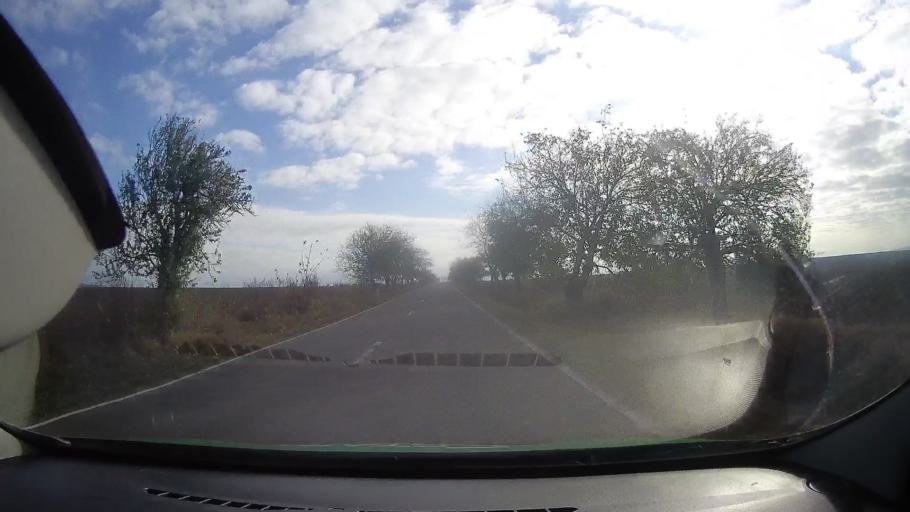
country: RO
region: Tulcea
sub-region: Comuna Bestepe
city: Bestepe
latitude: 45.0795
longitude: 29.0388
